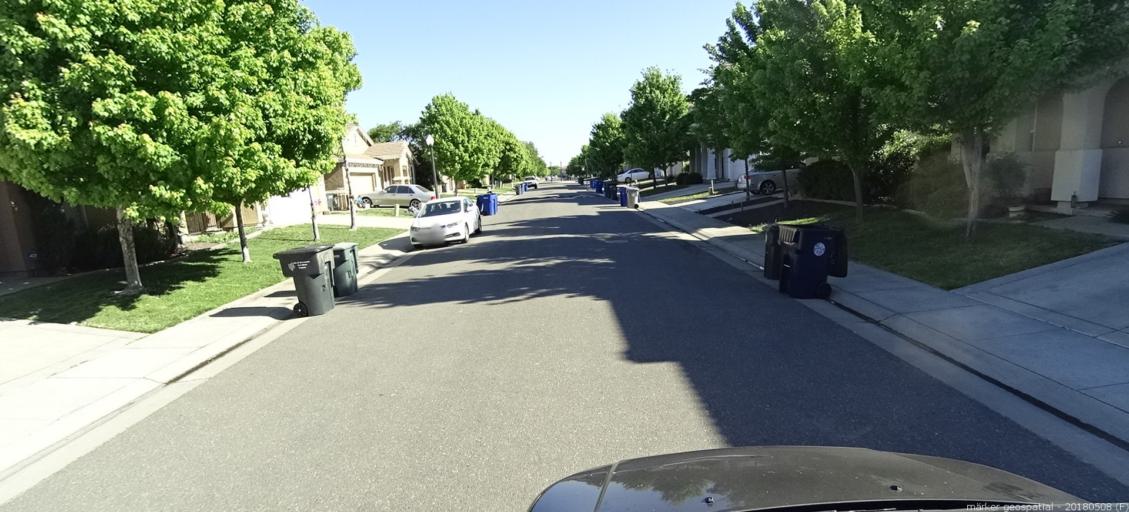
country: US
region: California
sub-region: Sacramento County
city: Rio Linda
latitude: 38.6783
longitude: -121.4939
